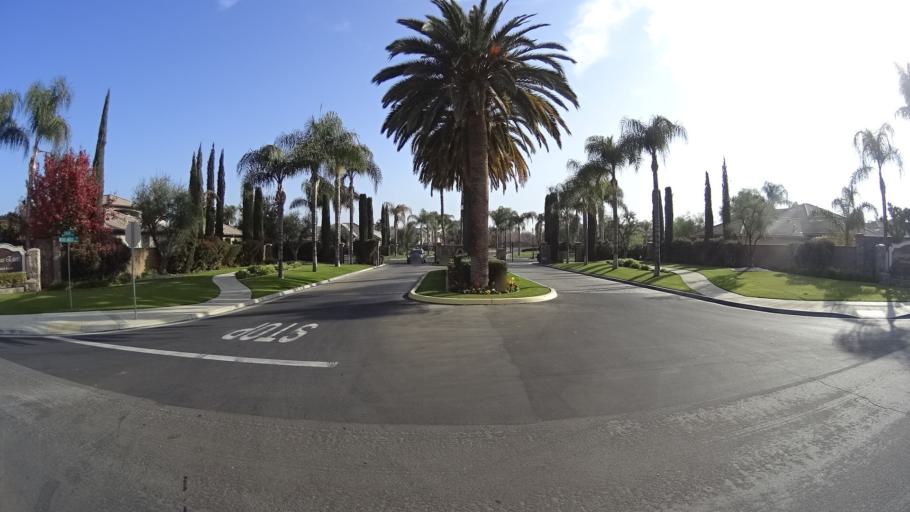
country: US
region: California
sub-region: Kern County
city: Rosedale
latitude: 35.3708
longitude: -119.1544
